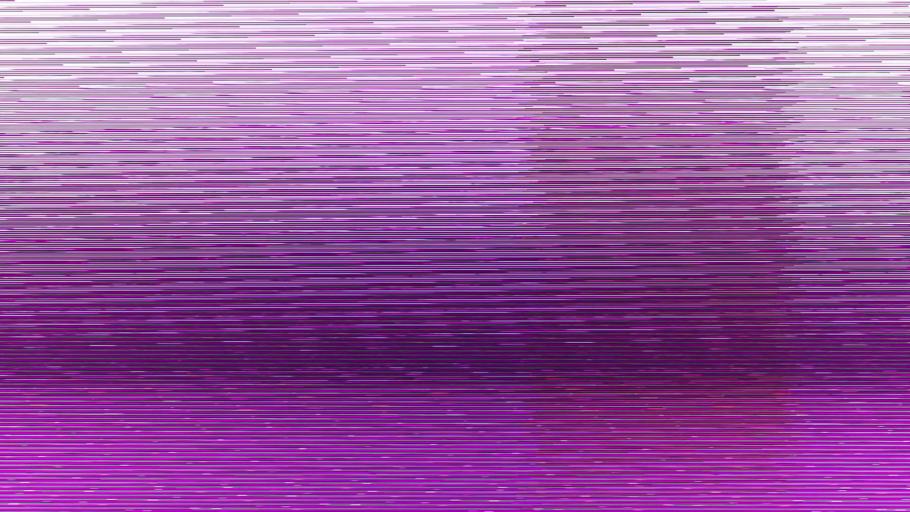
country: US
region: Michigan
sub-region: Washtenaw County
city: Ann Arbor
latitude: 42.2612
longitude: -83.7831
